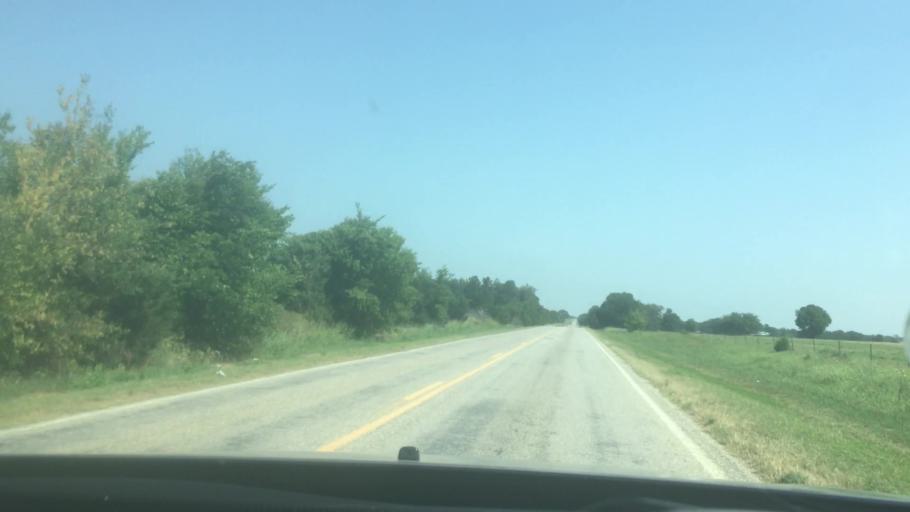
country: US
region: Oklahoma
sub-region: Johnston County
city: Tishomingo
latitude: 34.2847
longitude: -96.4248
